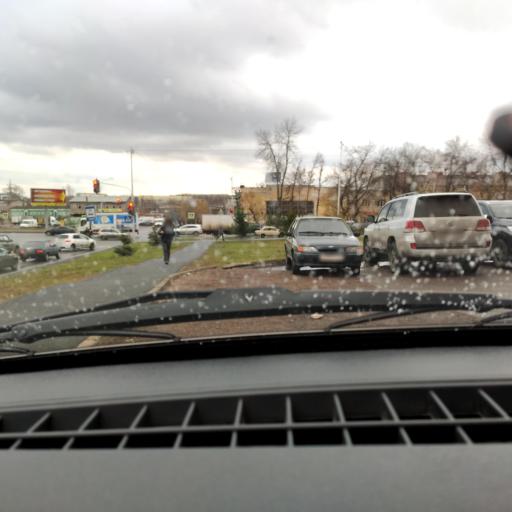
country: RU
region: Bashkortostan
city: Ufa
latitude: 54.8046
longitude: 56.1114
